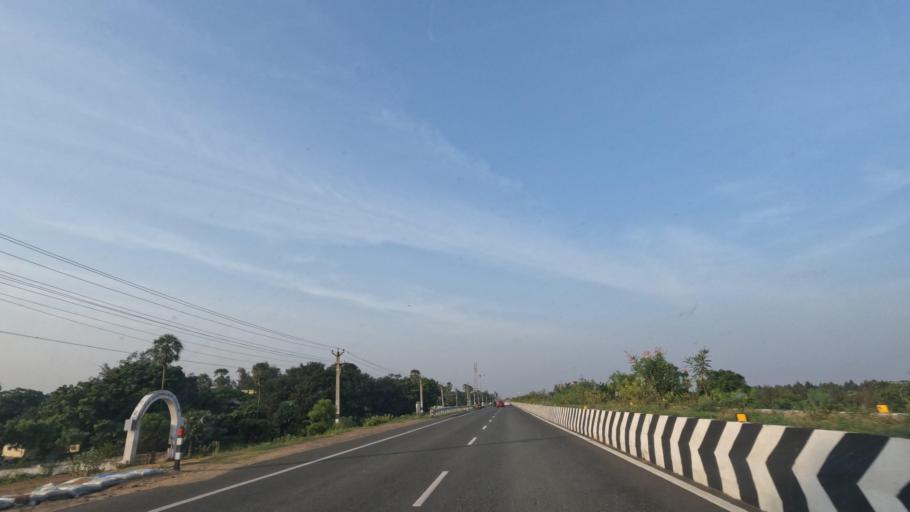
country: IN
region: Tamil Nadu
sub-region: Kancheepuram
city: Mamallapuram
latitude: 12.7201
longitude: 80.2287
